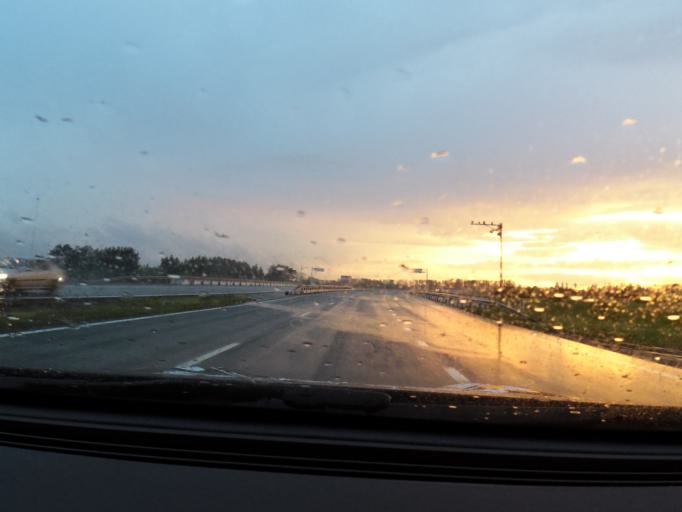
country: RU
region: Tatarstan
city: Yelabuga
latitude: 55.7819
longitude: 52.1782
